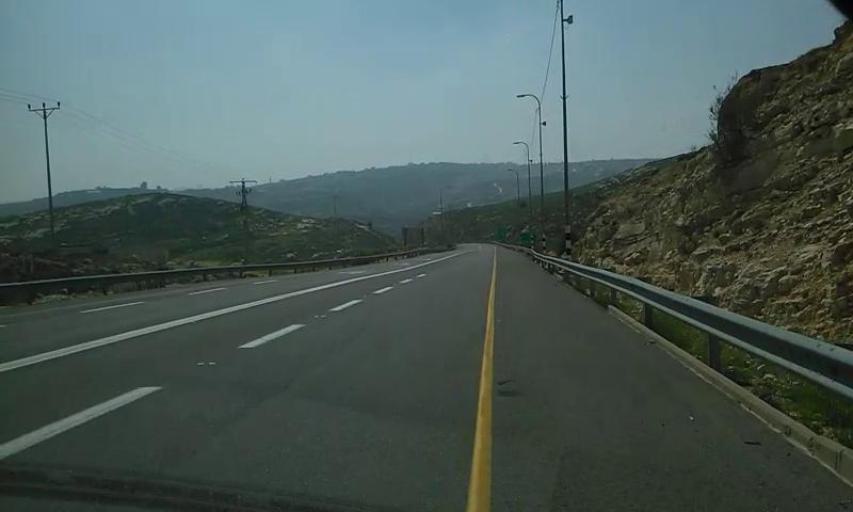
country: PS
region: West Bank
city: Mikhmas
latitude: 31.8785
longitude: 35.2674
